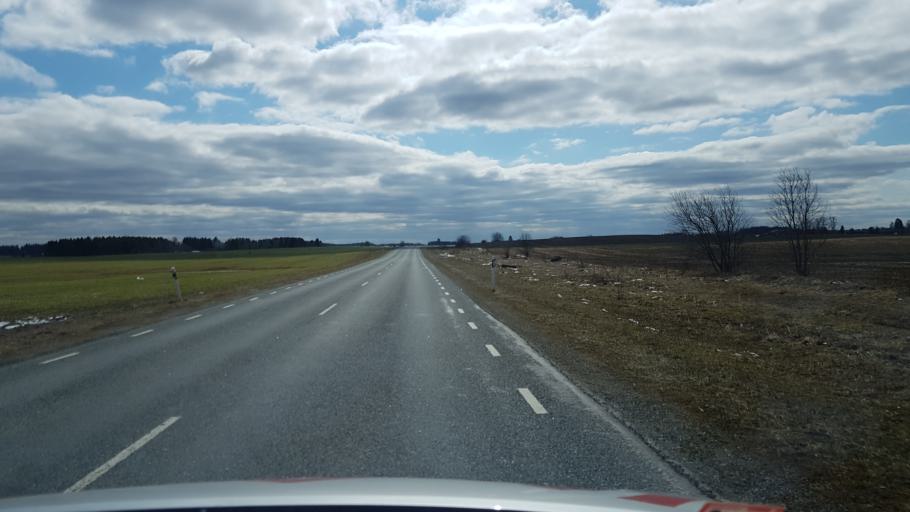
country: EE
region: Laeaene-Virumaa
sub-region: Tapa vald
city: Tapa
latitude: 59.3200
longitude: 26.0041
